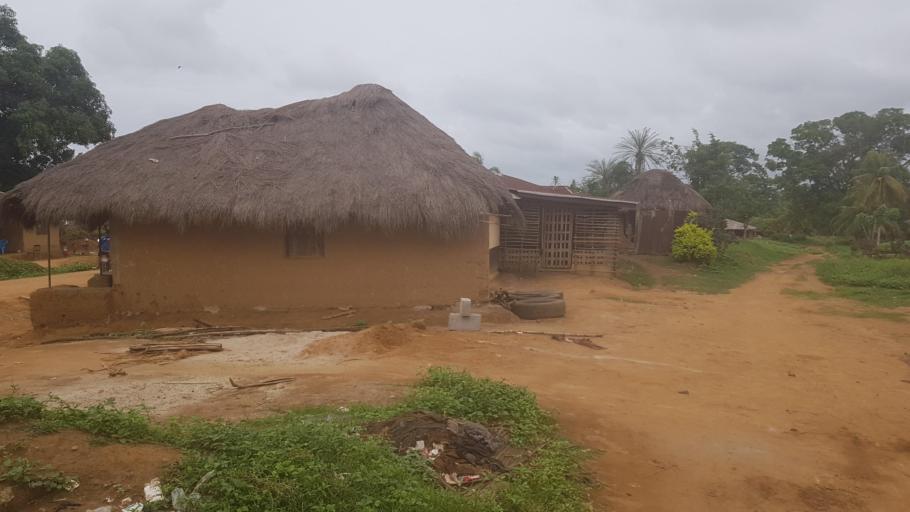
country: SL
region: Southern Province
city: Sumbuya
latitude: 7.5339
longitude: -12.1770
